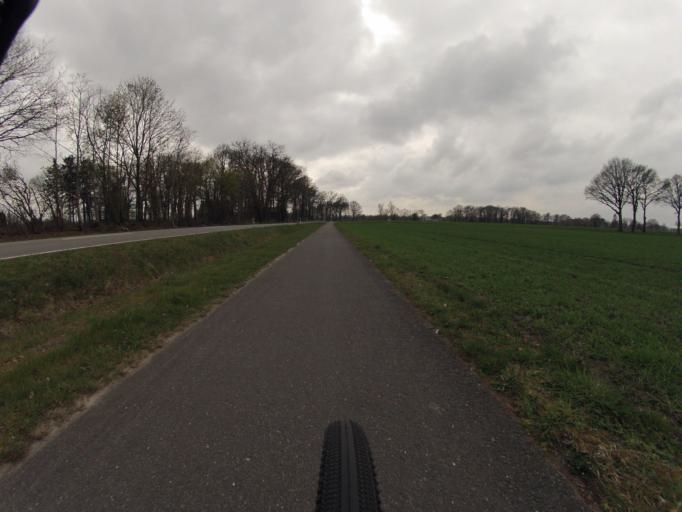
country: DE
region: North Rhine-Westphalia
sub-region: Regierungsbezirk Munster
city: Mettingen
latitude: 52.3474
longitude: 7.7912
